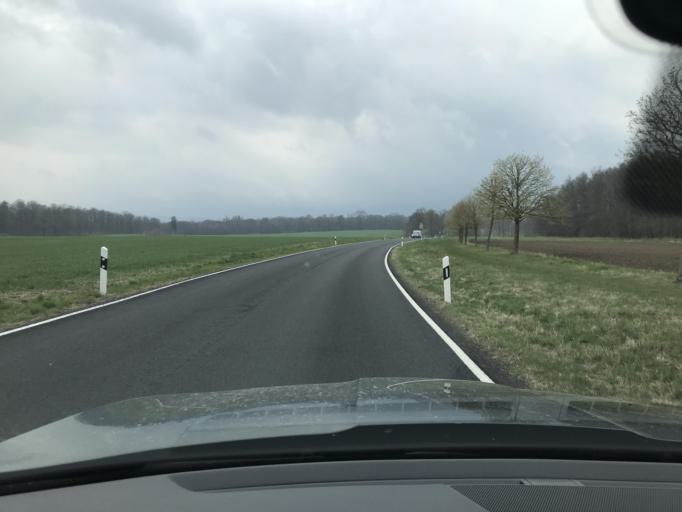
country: DE
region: Saxony-Anhalt
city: Harzgerode
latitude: 51.6534
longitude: 11.1371
